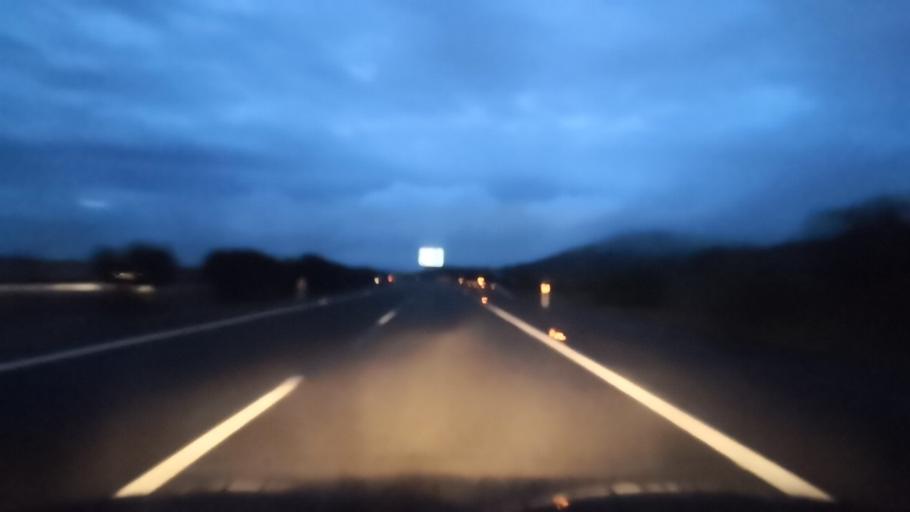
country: ES
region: Extremadura
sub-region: Provincia de Caceres
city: Caceres
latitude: 39.4173
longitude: -6.4017
